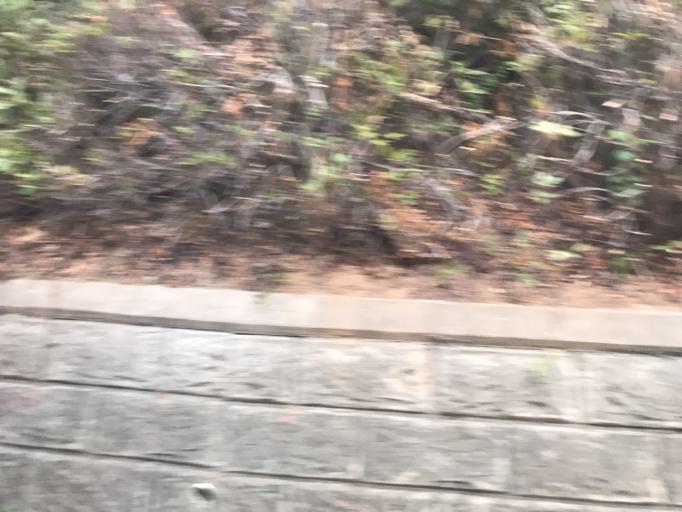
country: KR
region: Seoul
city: Seoul
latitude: 37.5665
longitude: 126.9461
